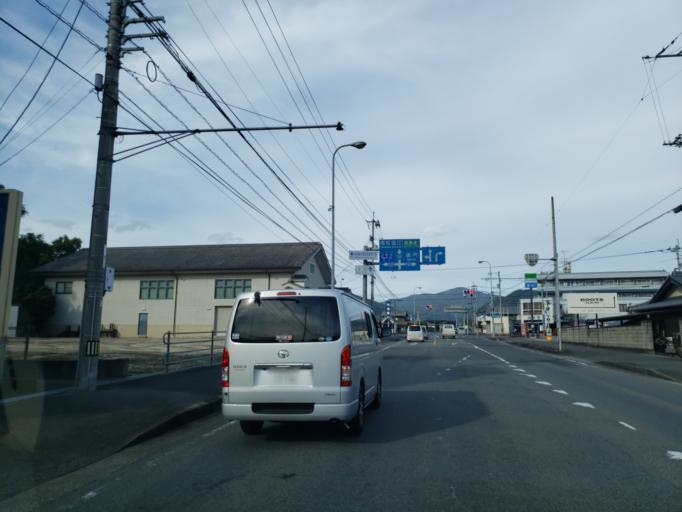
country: JP
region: Tokushima
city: Wakimachi
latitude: 34.0650
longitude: 134.1695
